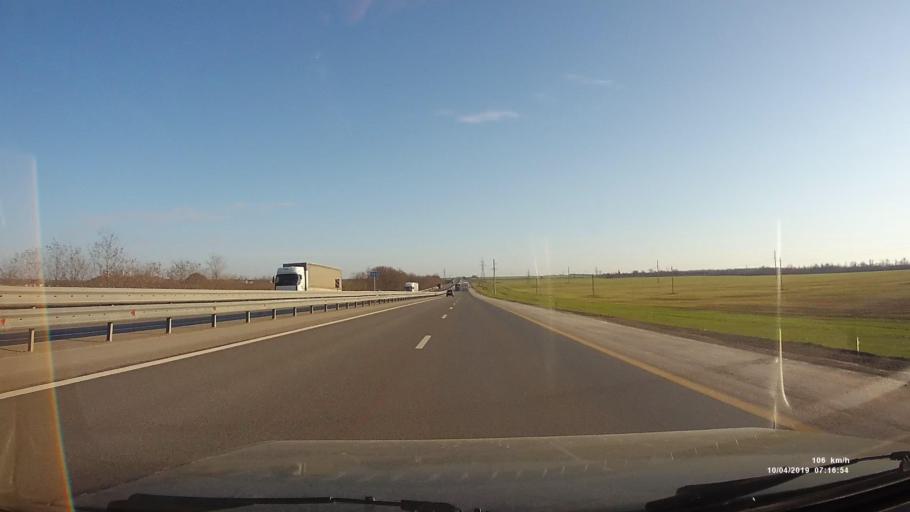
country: RU
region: Rostov
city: Ayutinskiy
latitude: 47.7765
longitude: 40.1600
